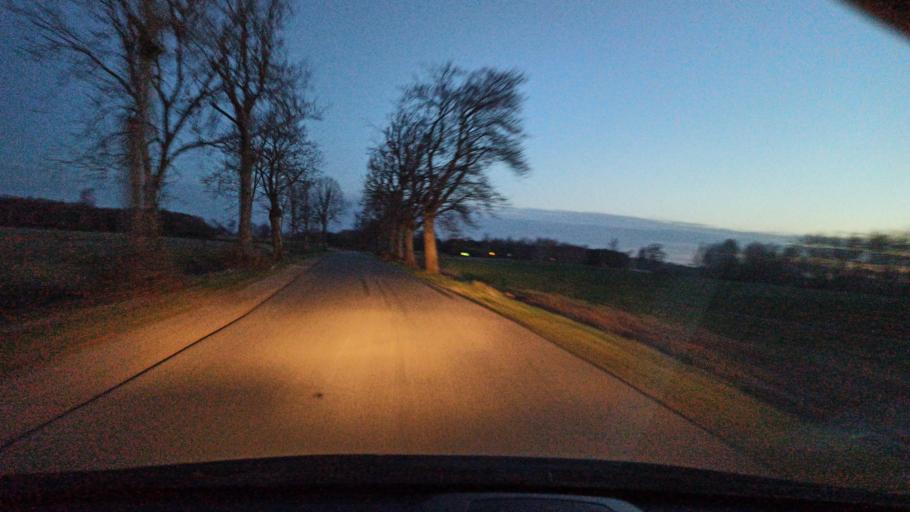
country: PL
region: Warmian-Masurian Voivodeship
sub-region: Powiat elblaski
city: Gronowo Gorne
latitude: 54.1768
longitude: 19.5162
